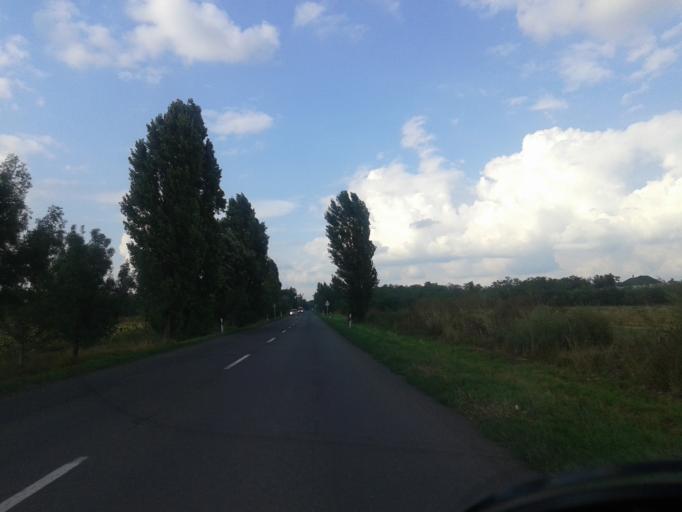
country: HU
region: Pest
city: Dunavarsany
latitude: 47.2555
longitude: 19.0256
